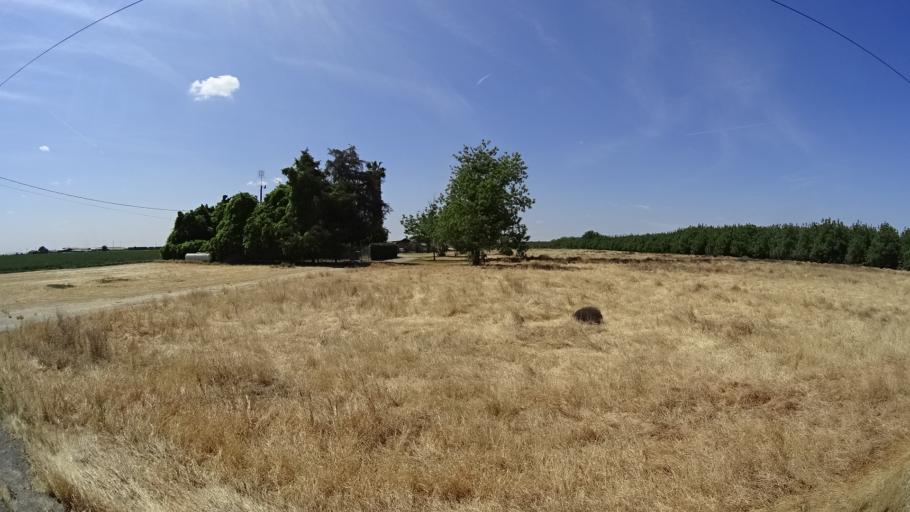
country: US
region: California
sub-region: Kings County
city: Armona
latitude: 36.2694
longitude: -119.6904
